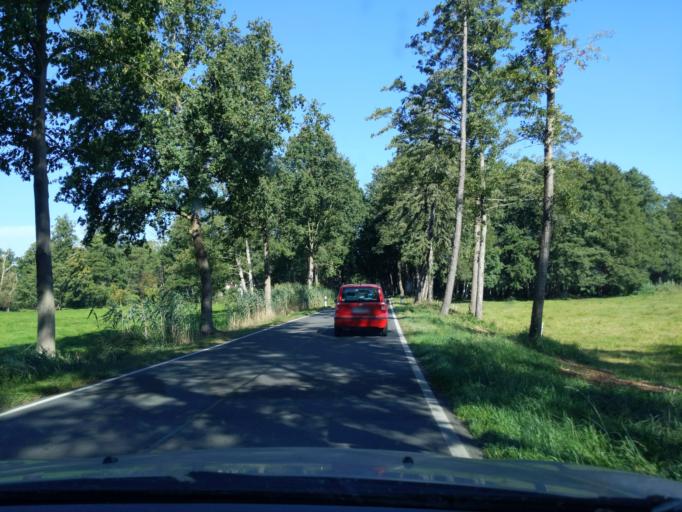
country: DE
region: Brandenburg
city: Vetschau
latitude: 51.8247
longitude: 14.1038
